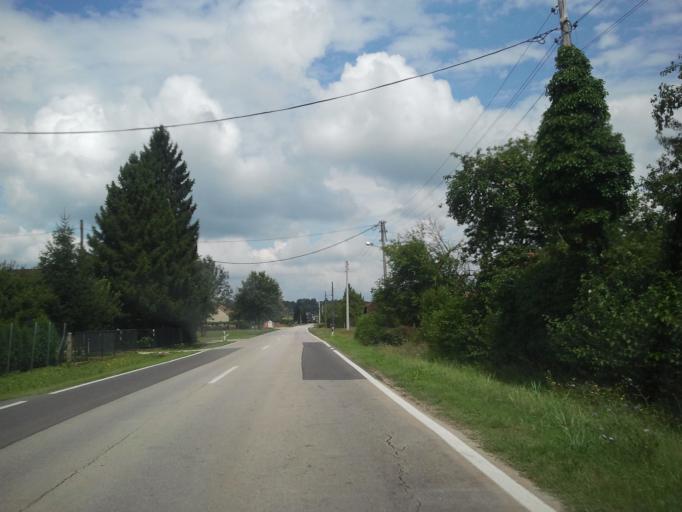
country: HR
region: Karlovacka
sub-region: Grad Karlovac
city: Karlovac
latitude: 45.5569
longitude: 15.5771
